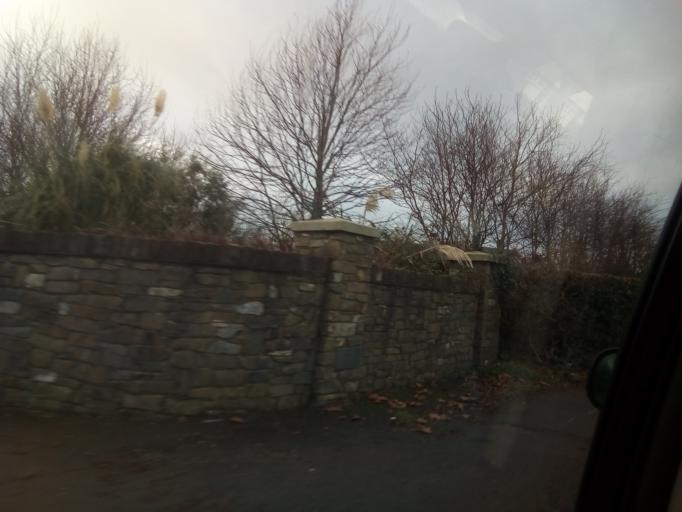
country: IE
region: Leinster
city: An Ros
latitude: 53.5419
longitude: -6.0958
